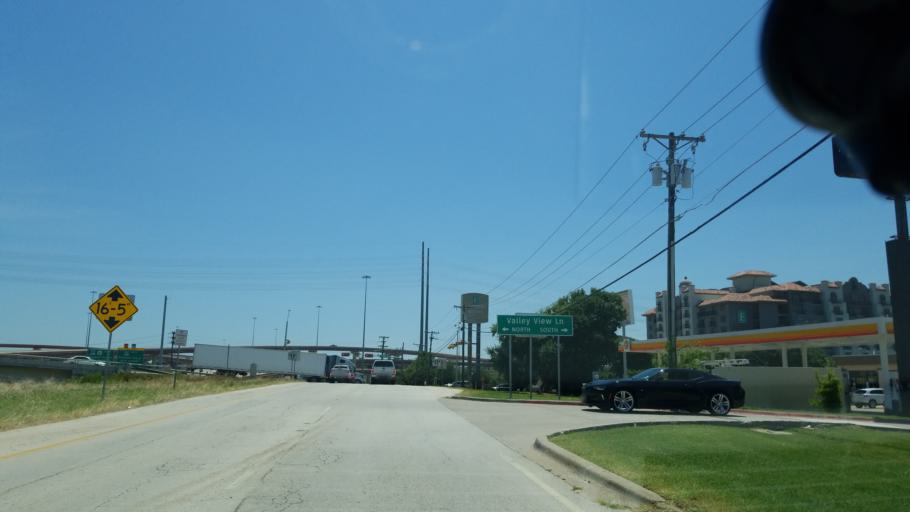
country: US
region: Texas
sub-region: Tarrant County
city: Euless
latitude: 32.8364
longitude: -97.0232
